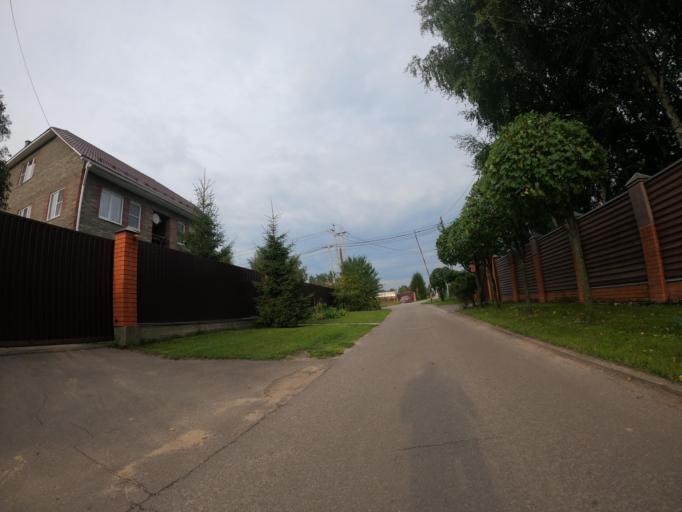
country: RU
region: Moskovskaya
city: Bykovo
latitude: 55.6550
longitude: 38.1038
